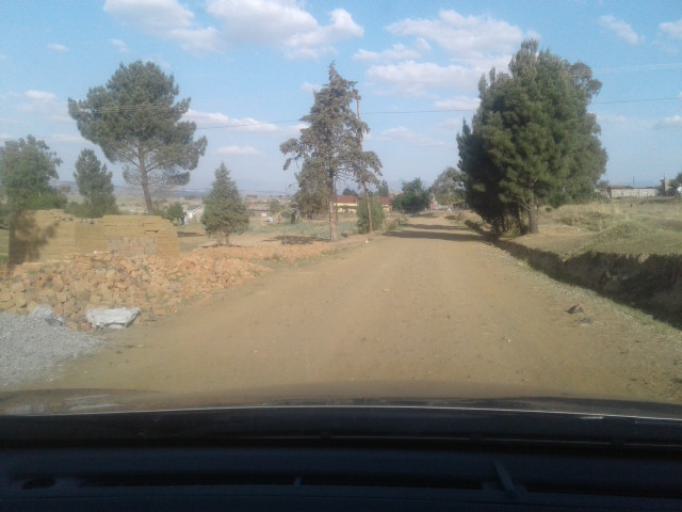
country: LS
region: Berea
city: Teyateyaneng
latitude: -29.1540
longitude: 27.7548
